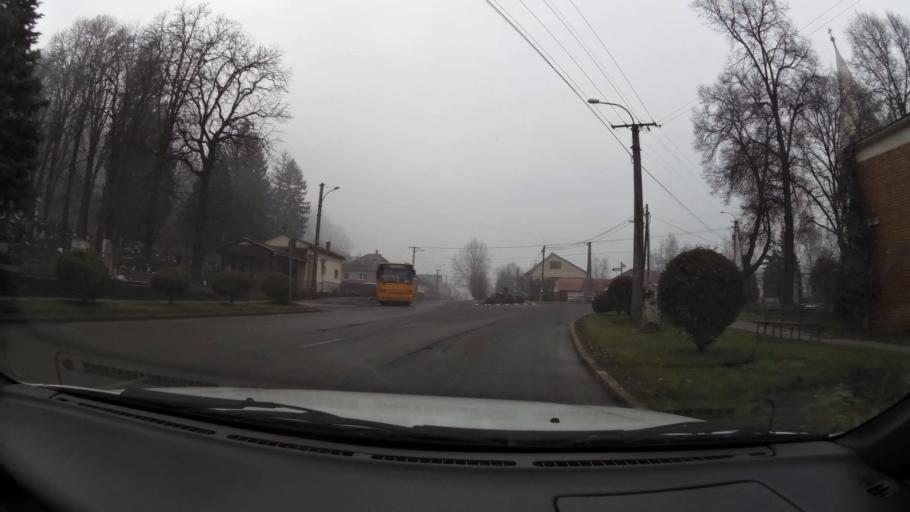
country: HU
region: Borsod-Abauj-Zemplen
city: Rudabanya
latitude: 48.3760
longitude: 20.6196
